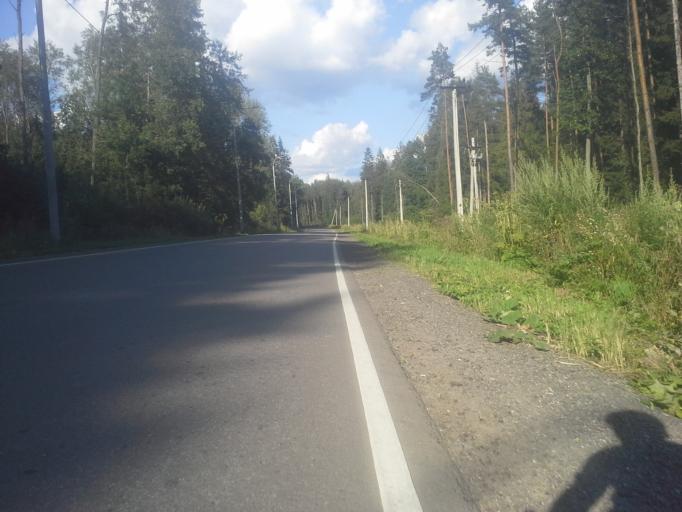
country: RU
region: Moskovskaya
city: Selyatino
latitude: 55.3989
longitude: 36.9900
